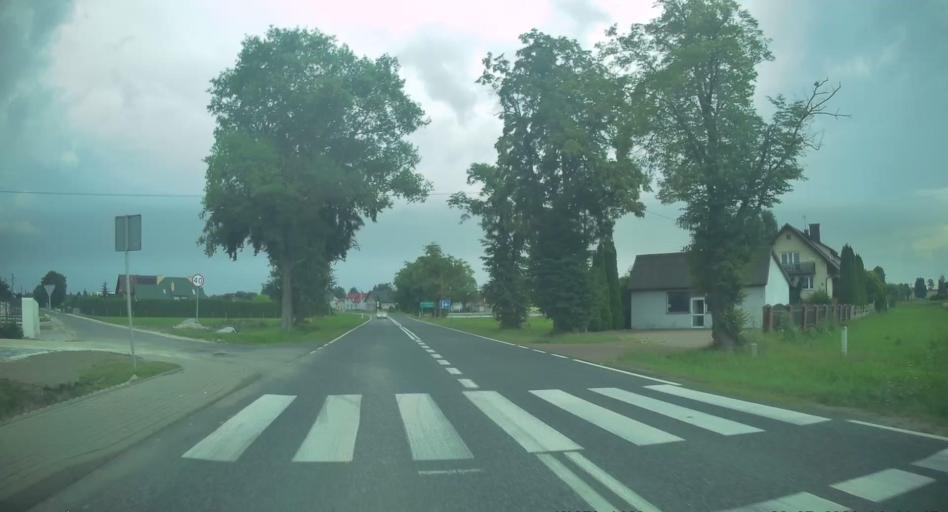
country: PL
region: Lodz Voivodeship
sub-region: Powiat skierniewicki
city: Gluchow
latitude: 51.7803
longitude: 20.0633
